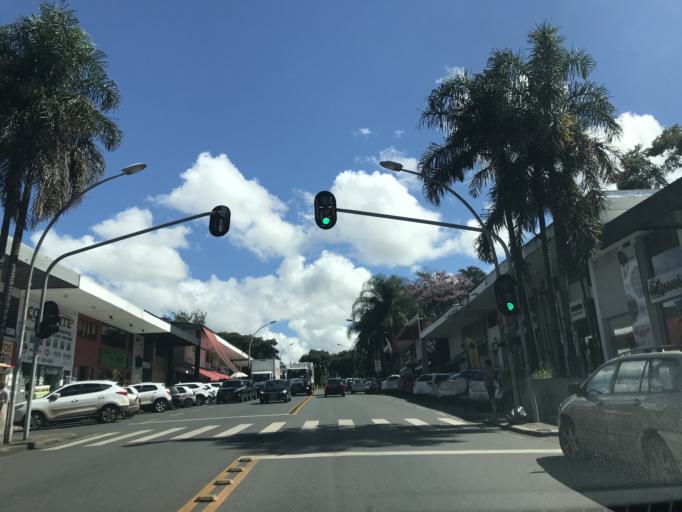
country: BR
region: Federal District
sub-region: Brasilia
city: Brasilia
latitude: -15.8230
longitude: -47.9009
